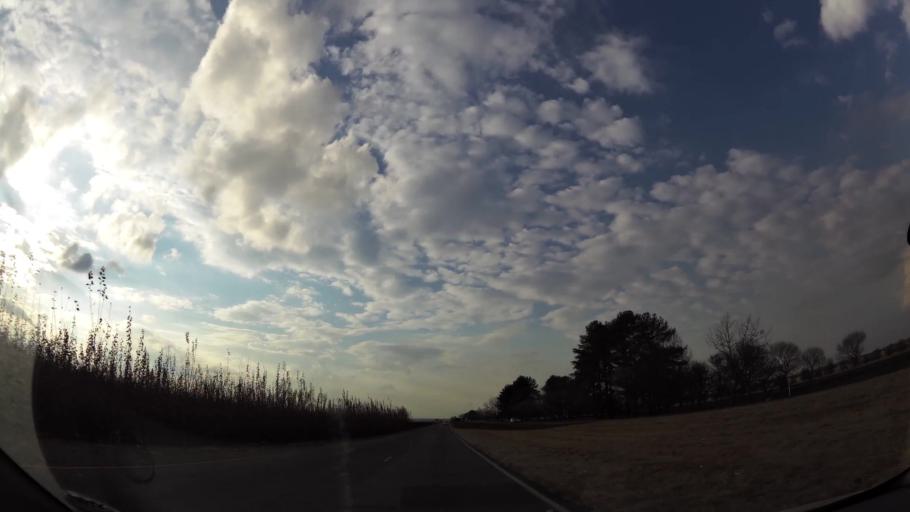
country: ZA
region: Orange Free State
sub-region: Fezile Dabi District Municipality
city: Sasolburg
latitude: -26.7838
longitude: 27.8240
